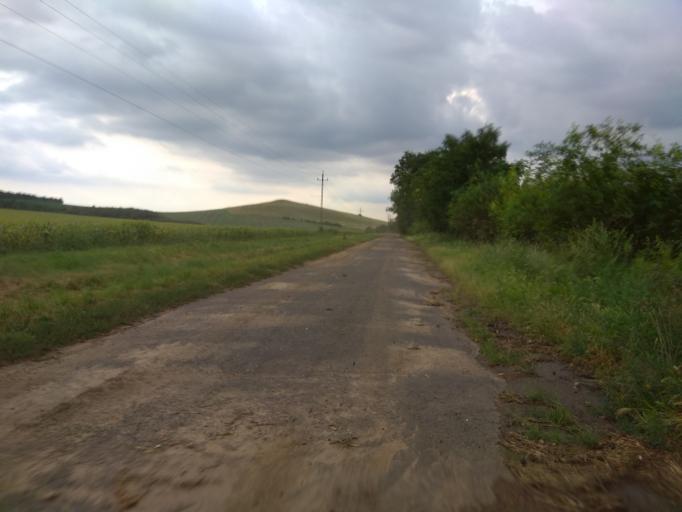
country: HU
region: Borsod-Abauj-Zemplen
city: Monok
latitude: 48.1889
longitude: 21.1256
